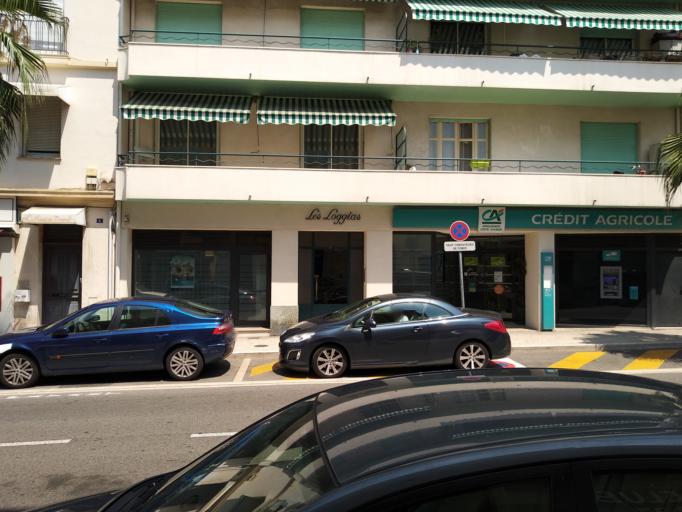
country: FR
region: Provence-Alpes-Cote d'Azur
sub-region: Departement des Alpes-Maritimes
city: Le Cannet
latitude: 43.5759
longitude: 7.0210
